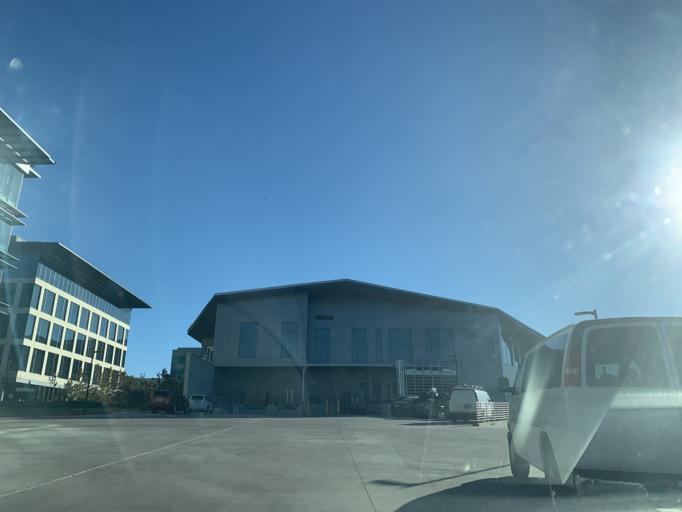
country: US
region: Texas
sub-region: Travis County
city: Wells Branch
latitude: 30.4010
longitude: -97.7124
